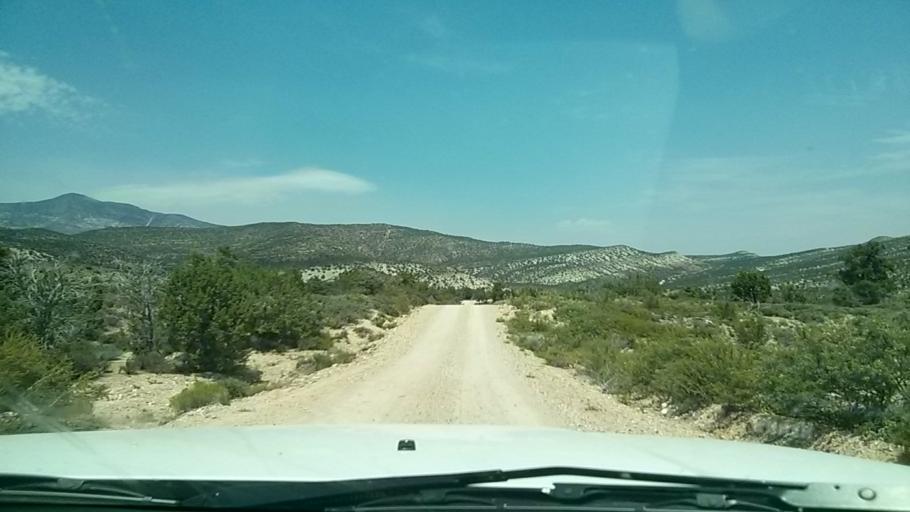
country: US
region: Utah
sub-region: Washington County
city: Washington
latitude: 37.2482
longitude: -113.4349
